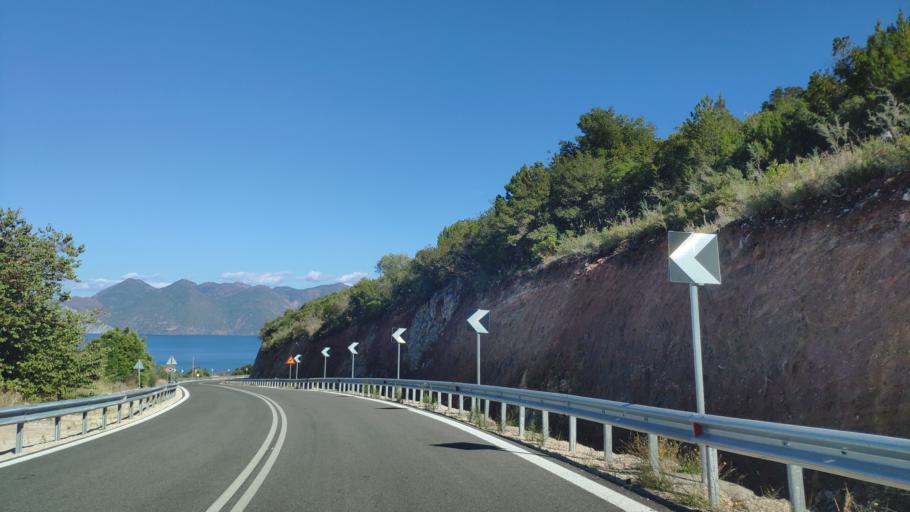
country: GR
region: Peloponnese
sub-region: Nomos Argolidos
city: Didyma
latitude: 37.5536
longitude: 23.2675
